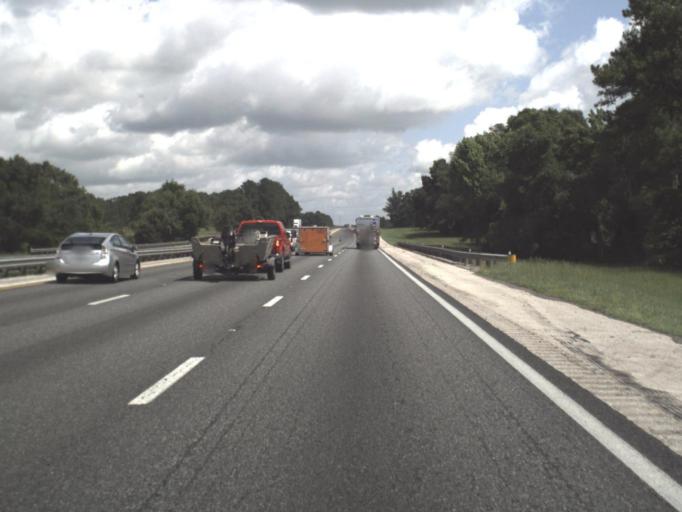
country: US
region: Florida
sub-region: Alachua County
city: High Springs
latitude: 29.9125
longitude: -82.5524
